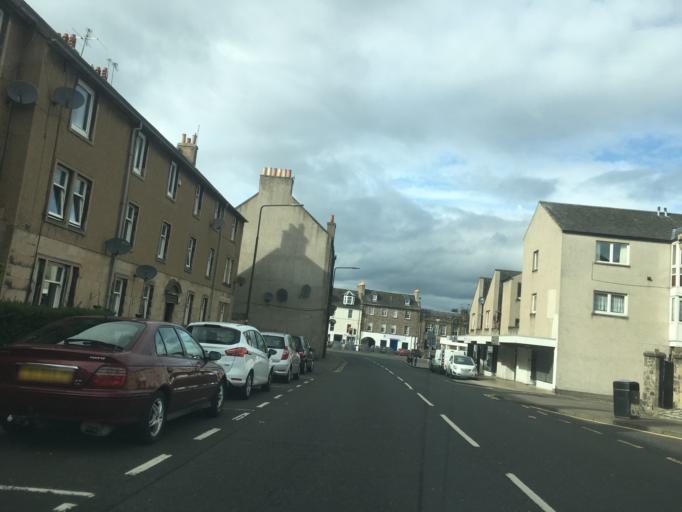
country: GB
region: Scotland
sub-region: East Lothian
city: Musselburgh
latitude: 55.9423
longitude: -3.0478
